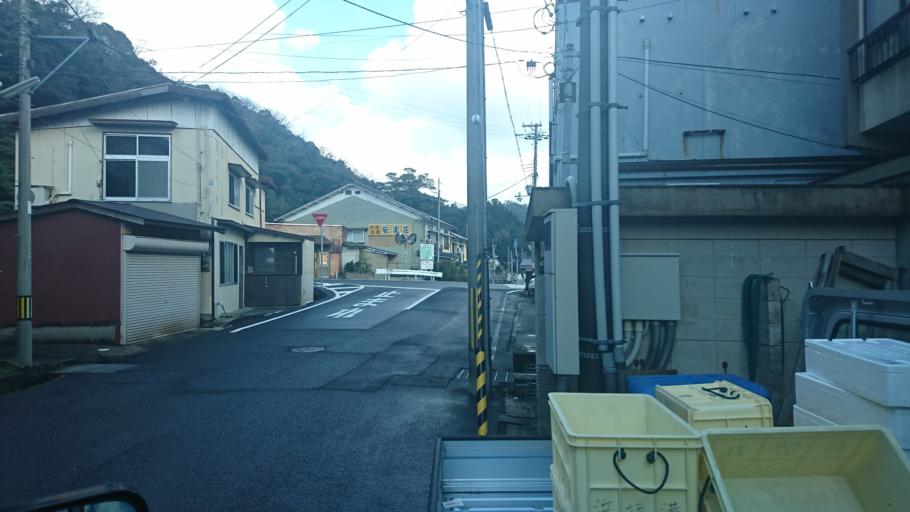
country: JP
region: Tottori
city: Tottori
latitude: 35.6104
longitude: 134.4756
